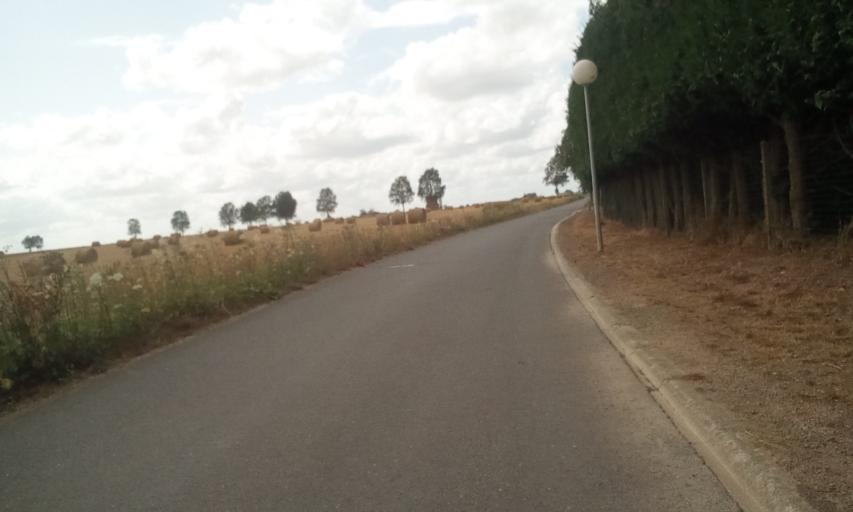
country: FR
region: Lower Normandy
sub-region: Departement du Calvados
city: Ver-sur-Mer
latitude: 49.3073
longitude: -0.4953
